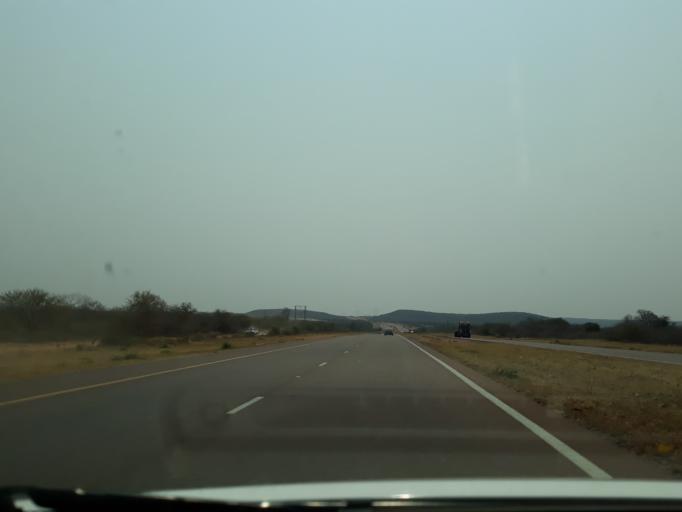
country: BW
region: Kgatleng
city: Bokaa
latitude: -24.4119
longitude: 26.0510
